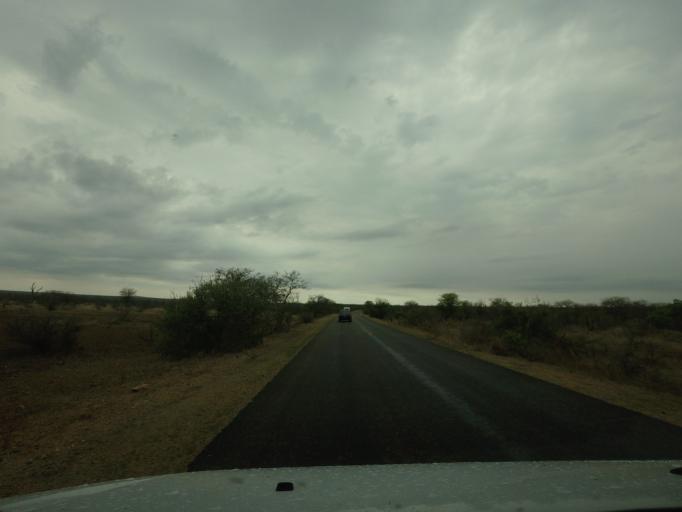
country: ZA
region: Limpopo
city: Thulamahashi
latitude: -24.4735
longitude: 31.4062
